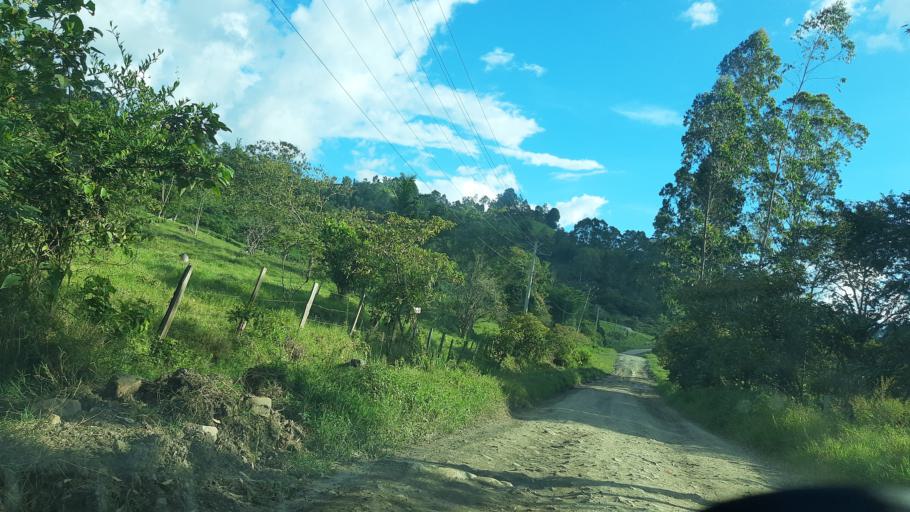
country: CO
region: Boyaca
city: Garagoa
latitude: 5.0823
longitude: -73.3709
